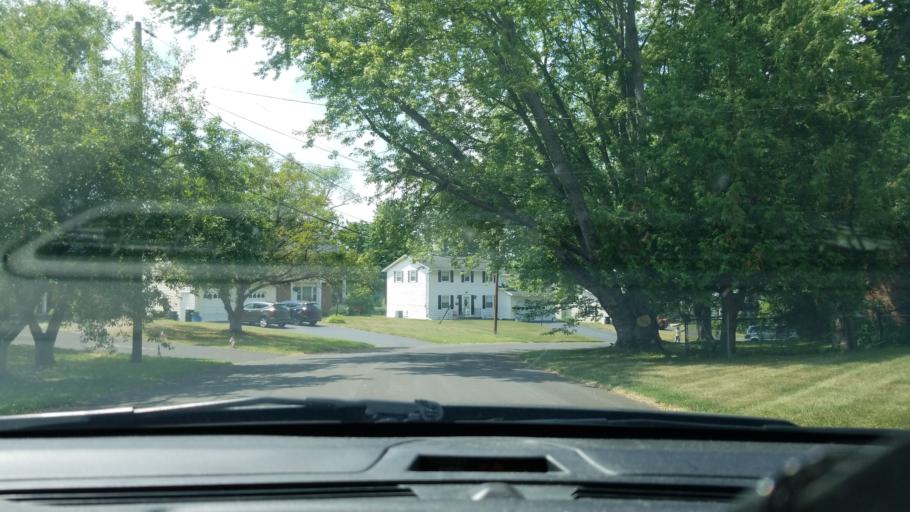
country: US
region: New York
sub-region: Onondaga County
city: Liverpool
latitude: 43.1388
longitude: -76.2359
